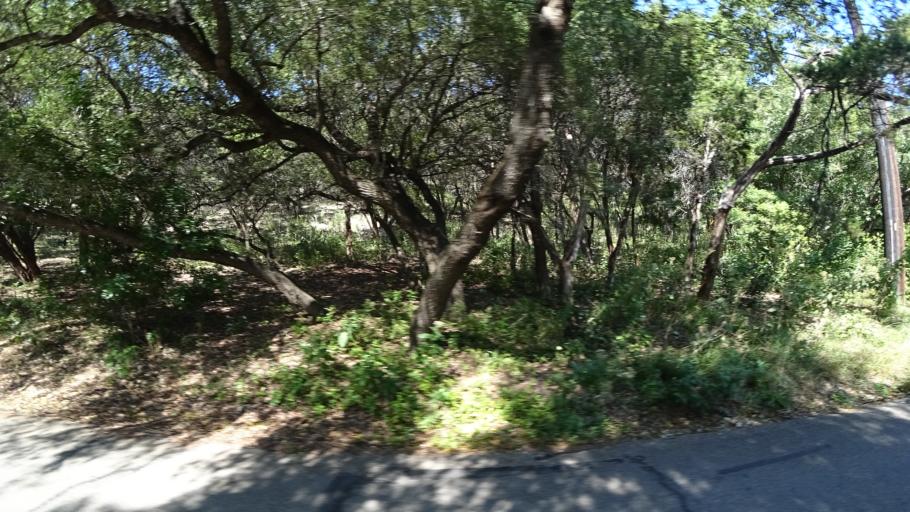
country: US
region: Texas
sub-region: Travis County
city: West Lake Hills
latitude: 30.2944
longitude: -97.8068
